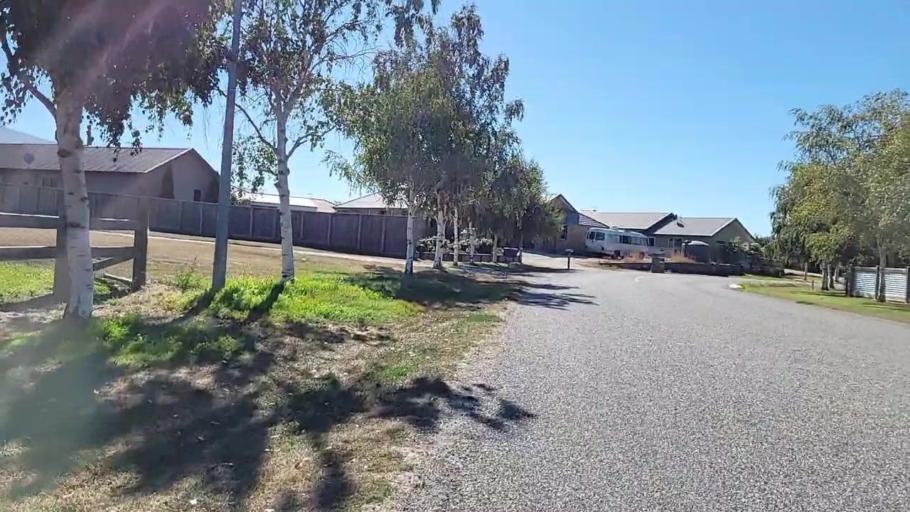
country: NZ
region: Otago
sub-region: Queenstown-Lakes District
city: Wanaka
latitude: -44.9739
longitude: 169.2443
